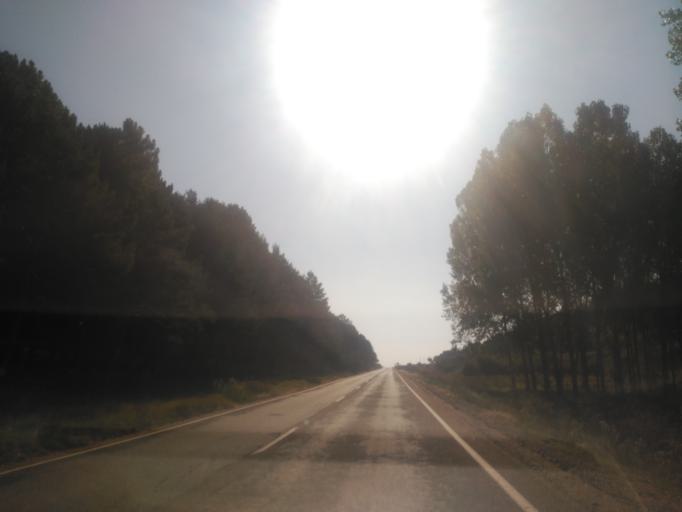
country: ES
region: Castille and Leon
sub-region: Provincia de Soria
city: Casarejos
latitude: 41.8081
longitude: -3.0549
